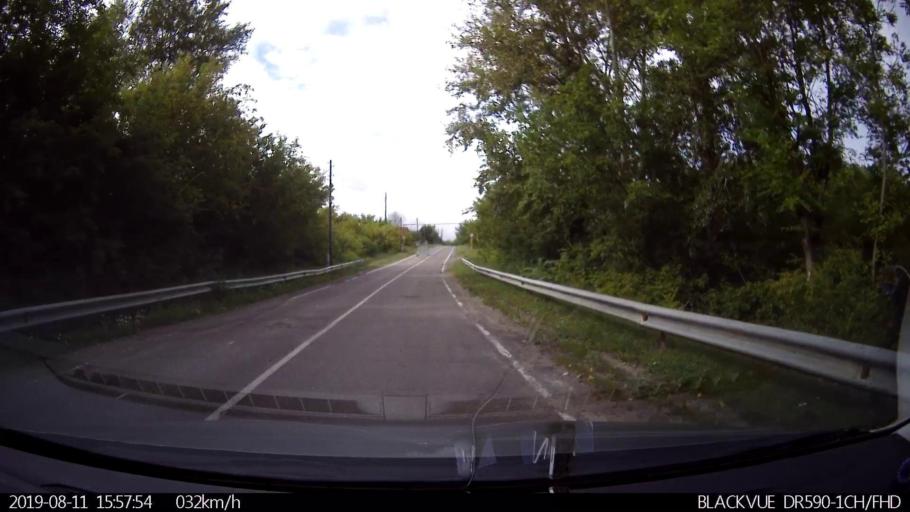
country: RU
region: Ulyanovsk
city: Ignatovka
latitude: 53.9531
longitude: 47.6507
